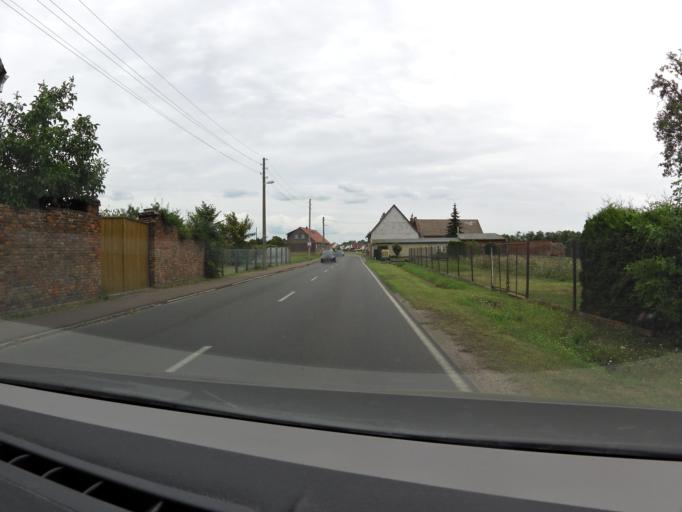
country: DE
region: Saxony-Anhalt
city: Worlitz
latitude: 51.8339
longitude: 12.4174
